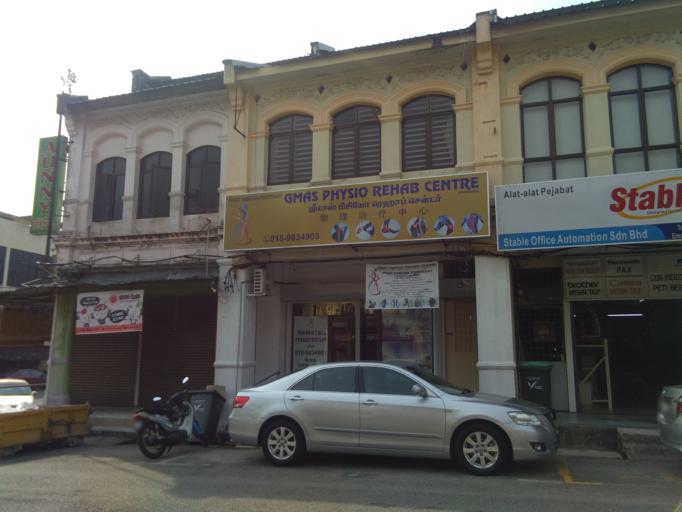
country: MY
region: Kedah
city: Kulim
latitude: 5.3705
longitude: 100.5544
